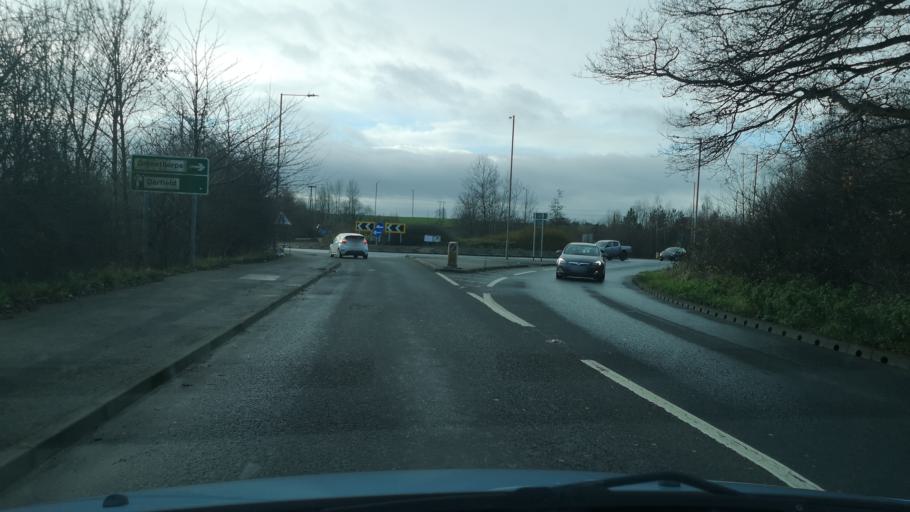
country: GB
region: England
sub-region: Barnsley
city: Little Houghton
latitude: 53.5382
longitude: -1.3526
